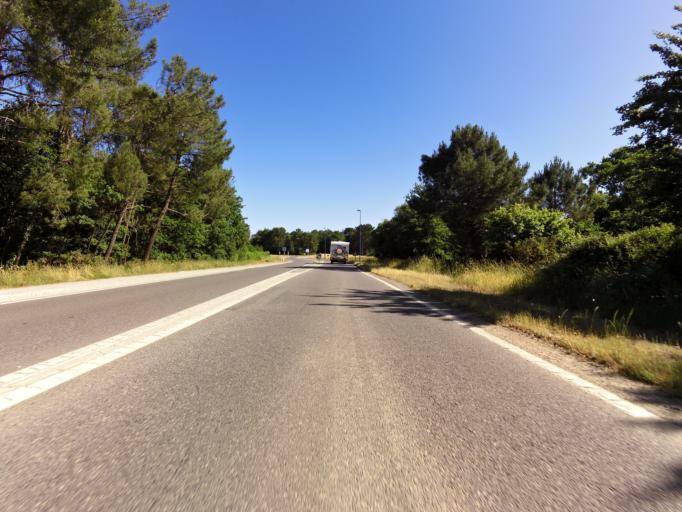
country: FR
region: Brittany
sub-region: Departement du Morbihan
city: Ferel
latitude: 47.4848
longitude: -2.3863
